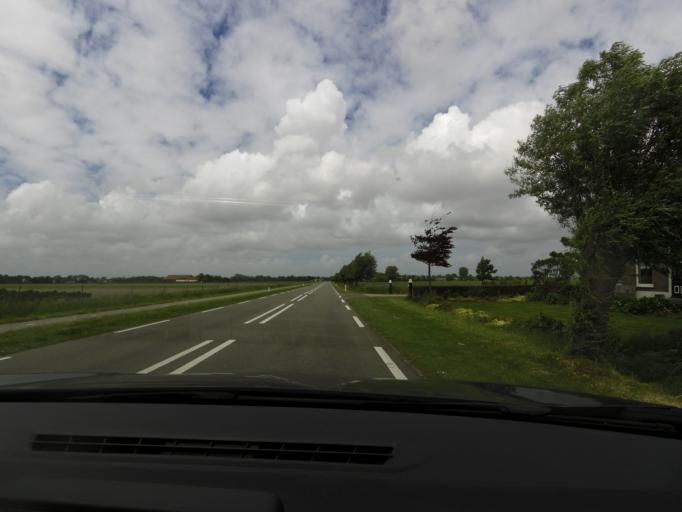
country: NL
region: Zeeland
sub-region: Schouwen-Duiveland
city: Scharendijke
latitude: 51.6856
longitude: 3.9409
